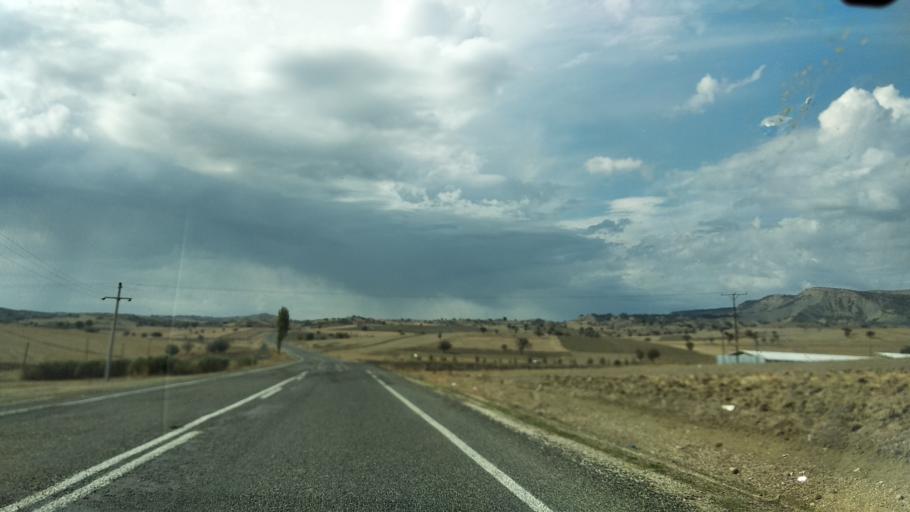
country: TR
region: Bolu
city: Seben
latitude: 40.3935
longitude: 31.5500
